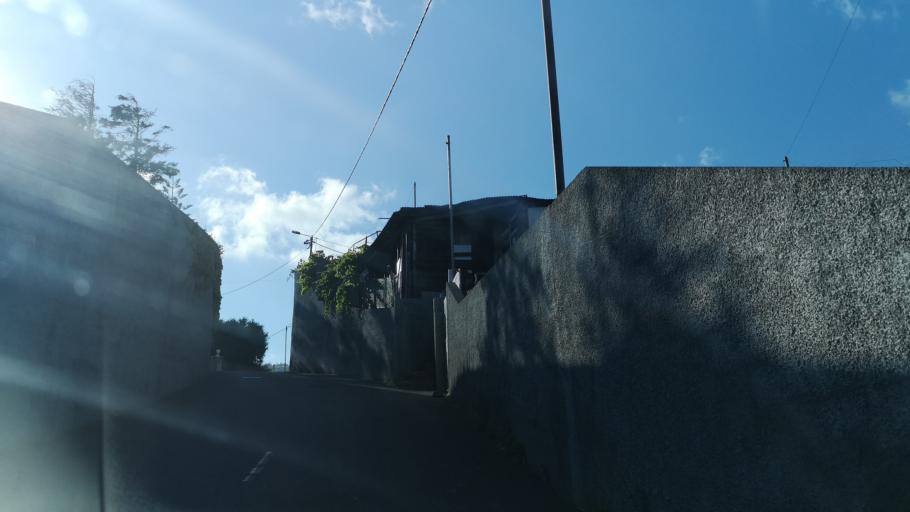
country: PT
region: Madeira
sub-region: Santa Cruz
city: Camacha
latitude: 32.6566
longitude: -16.8349
